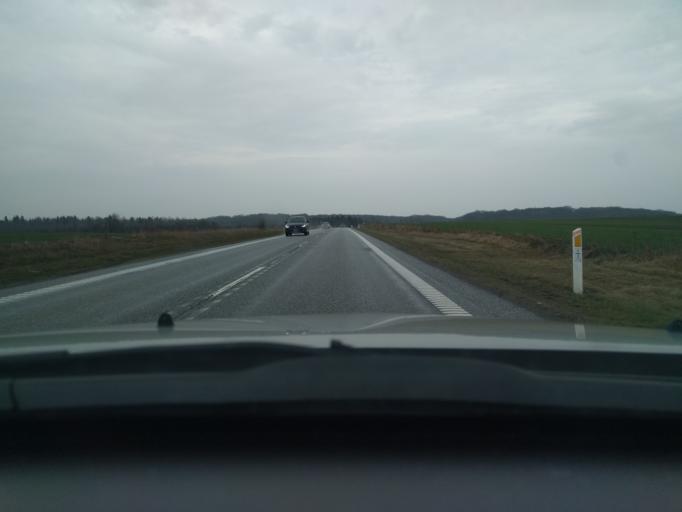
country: DK
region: Central Jutland
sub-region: Viborg Kommune
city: Viborg
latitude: 56.3929
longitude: 9.3240
